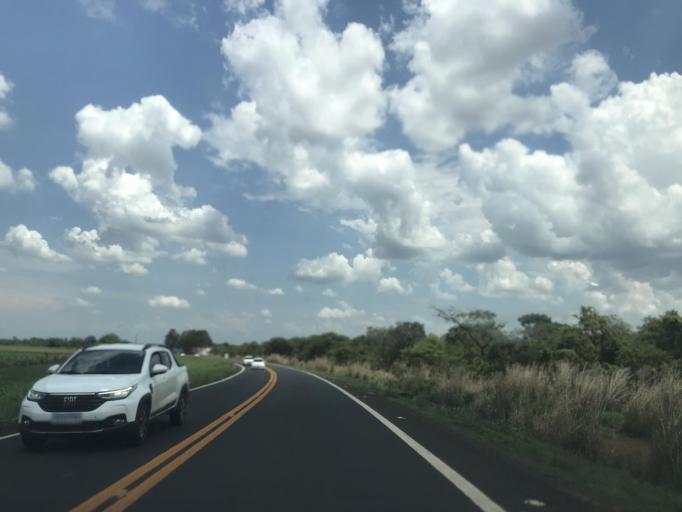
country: BR
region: Goias
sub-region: Piracanjuba
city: Piracanjuba
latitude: -17.4309
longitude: -48.8021
